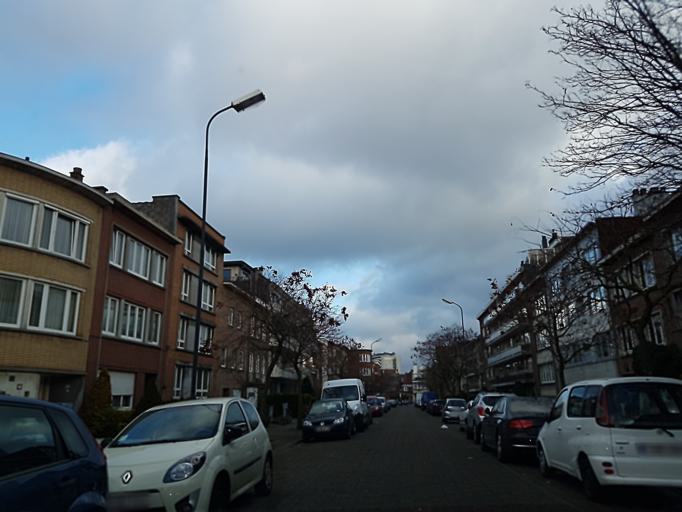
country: BE
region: Flanders
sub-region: Provincie Vlaams-Brabant
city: Diegem
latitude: 50.8716
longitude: 4.3979
